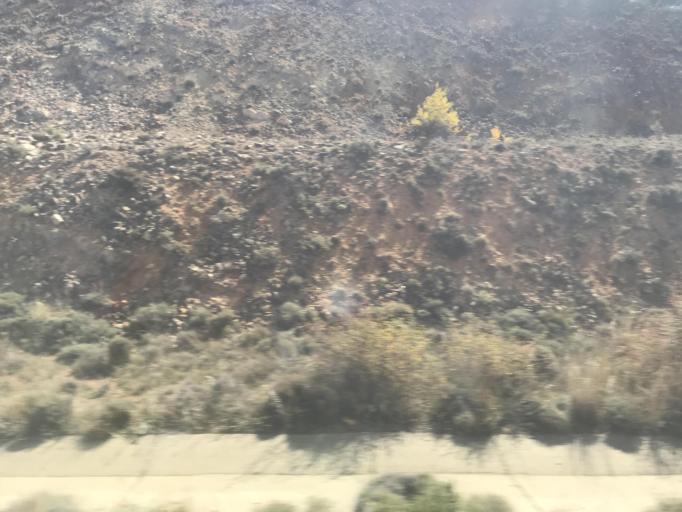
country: ES
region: Castille and Leon
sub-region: Provincia de Soria
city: Arcos de Jalon
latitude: 41.1449
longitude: -2.3137
